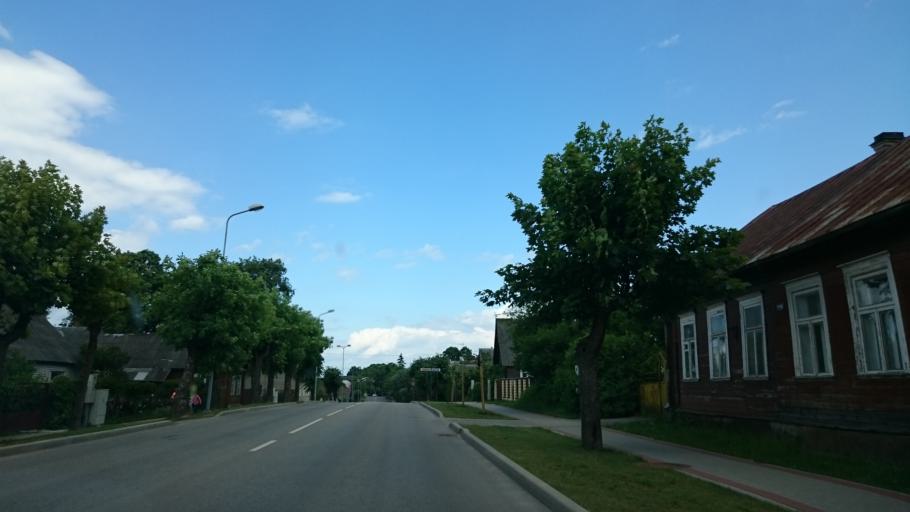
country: LV
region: Ludzas Rajons
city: Ludza
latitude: 56.5444
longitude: 27.7131
